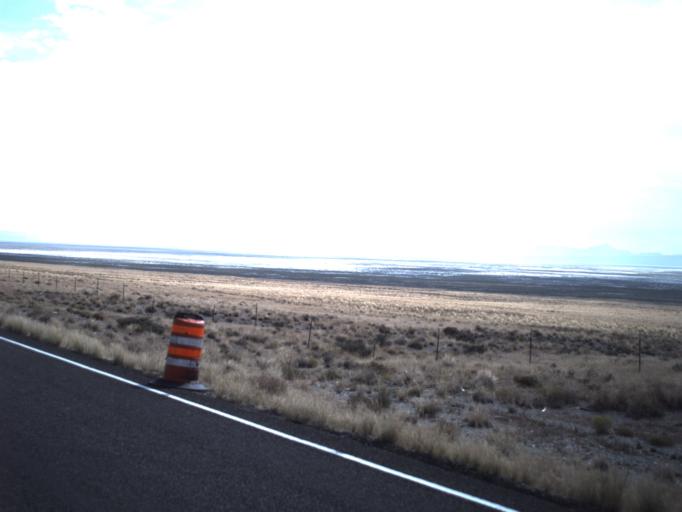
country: US
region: Utah
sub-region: Tooele County
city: Wendover
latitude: 41.4397
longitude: -113.7163
